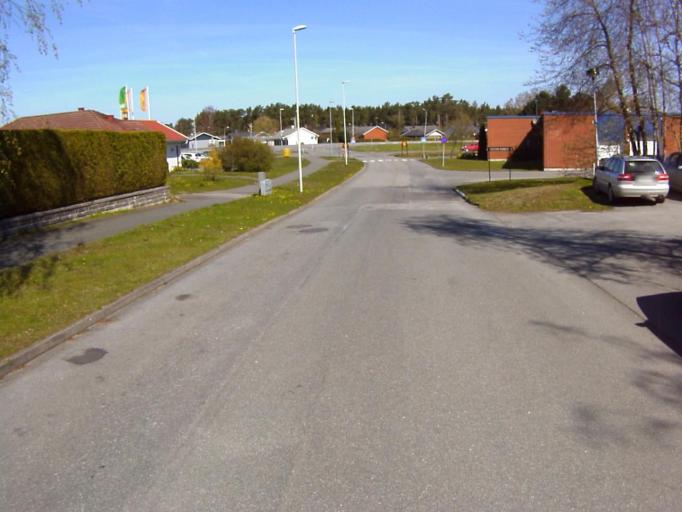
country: SE
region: Skane
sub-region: Kristianstads Kommun
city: Norra Asum
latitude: 56.0012
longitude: 14.0948
